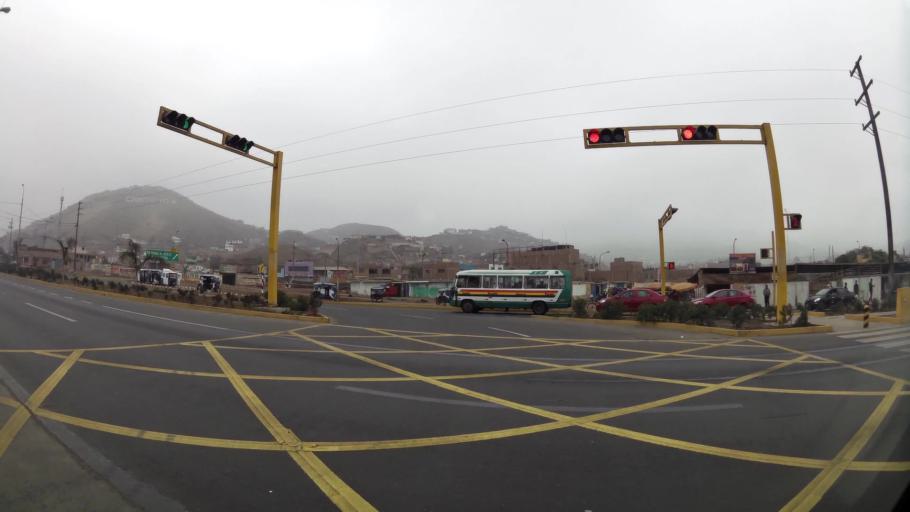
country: PE
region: Lima
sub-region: Lima
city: Santa Rosa
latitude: -11.8133
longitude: -77.1298
